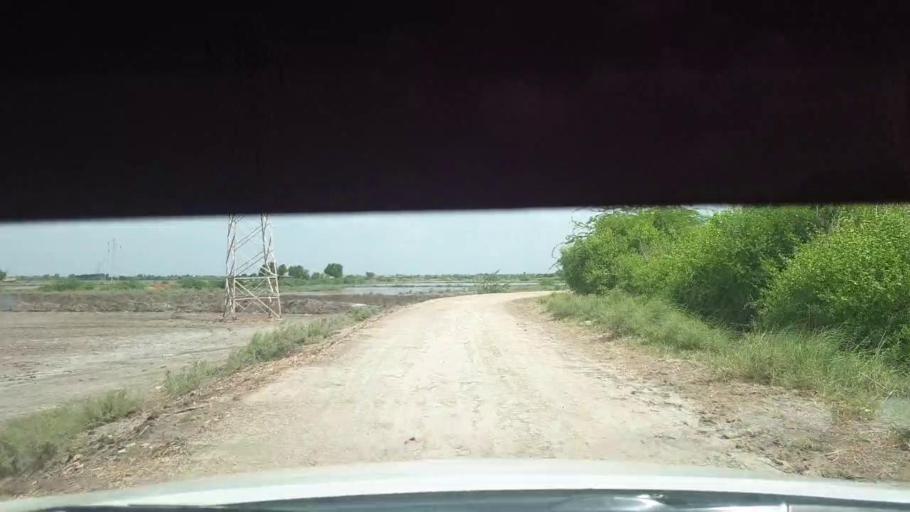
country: PK
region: Sindh
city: Kadhan
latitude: 24.4922
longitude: 68.9818
